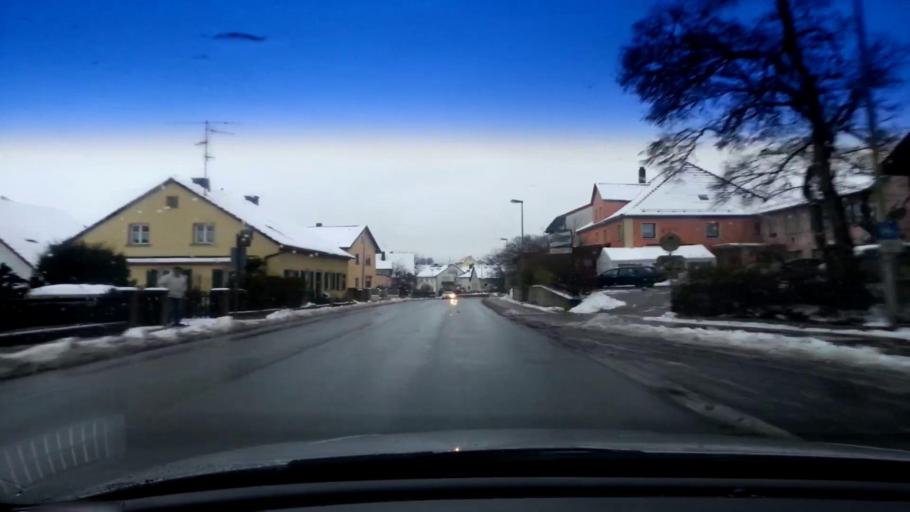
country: DE
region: Bavaria
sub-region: Upper Franconia
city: Litzendorf
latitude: 49.9110
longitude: 10.9871
